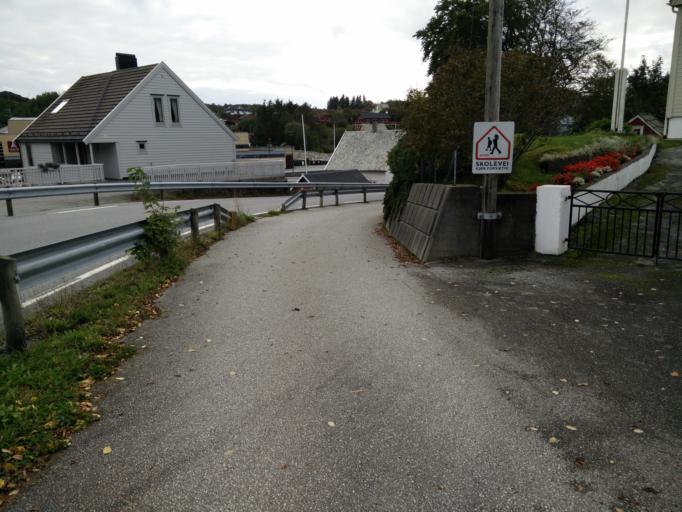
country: NO
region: Hordaland
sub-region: Sveio
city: Sveio
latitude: 59.6030
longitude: 5.2091
